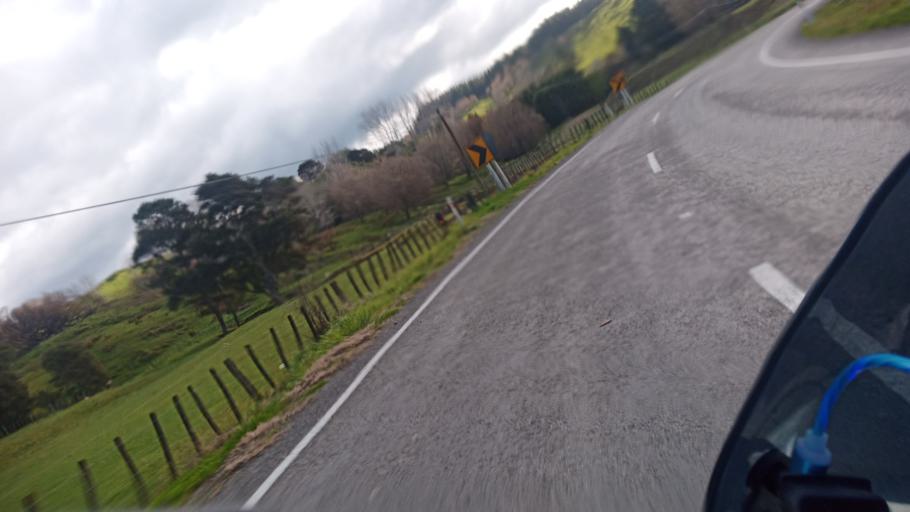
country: NZ
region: Gisborne
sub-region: Gisborne District
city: Gisborne
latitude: -38.0909
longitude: 178.2935
